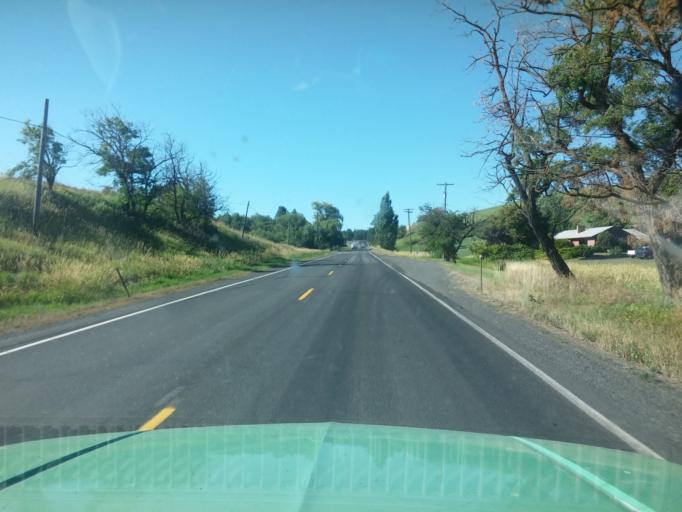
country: US
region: Idaho
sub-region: Latah County
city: Moscow
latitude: 46.7031
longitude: -117.0065
